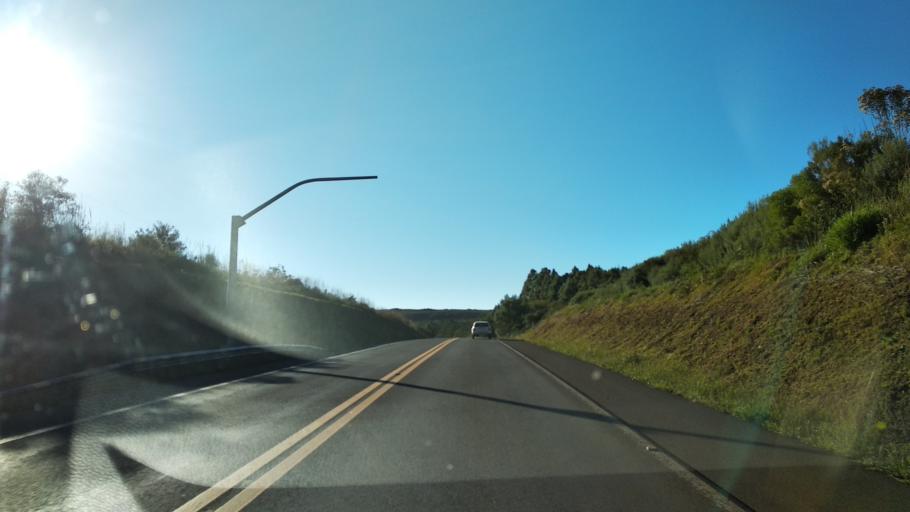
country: BR
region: Santa Catarina
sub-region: Lages
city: Lages
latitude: -27.7877
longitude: -50.4355
